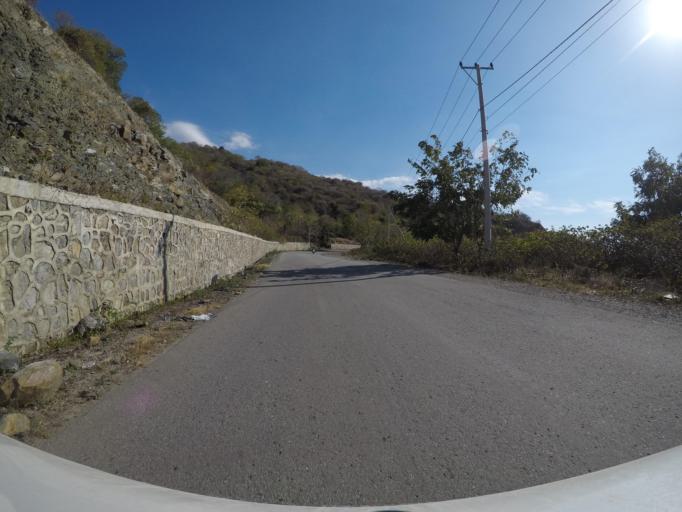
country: TL
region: Liquica
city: Maubara
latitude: -8.6261
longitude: 125.1617
